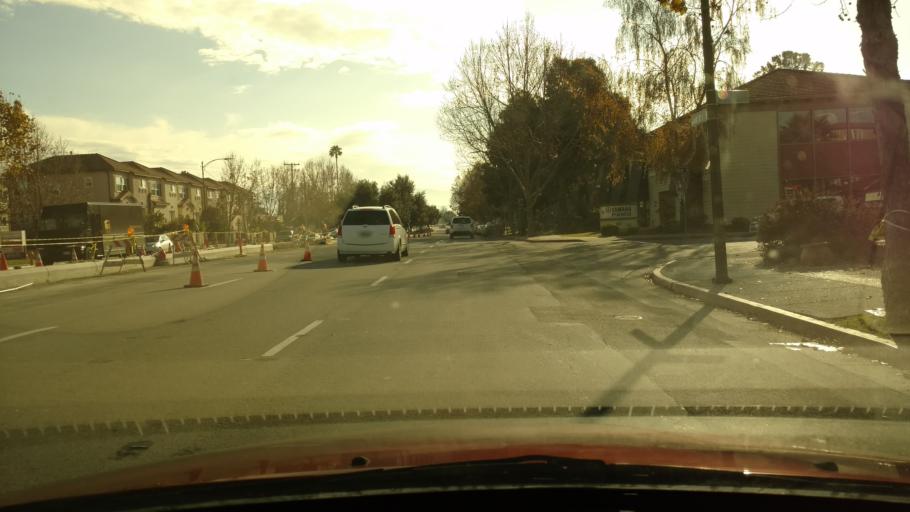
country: US
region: California
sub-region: Santa Clara County
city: Burbank
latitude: 37.3121
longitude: -121.9502
